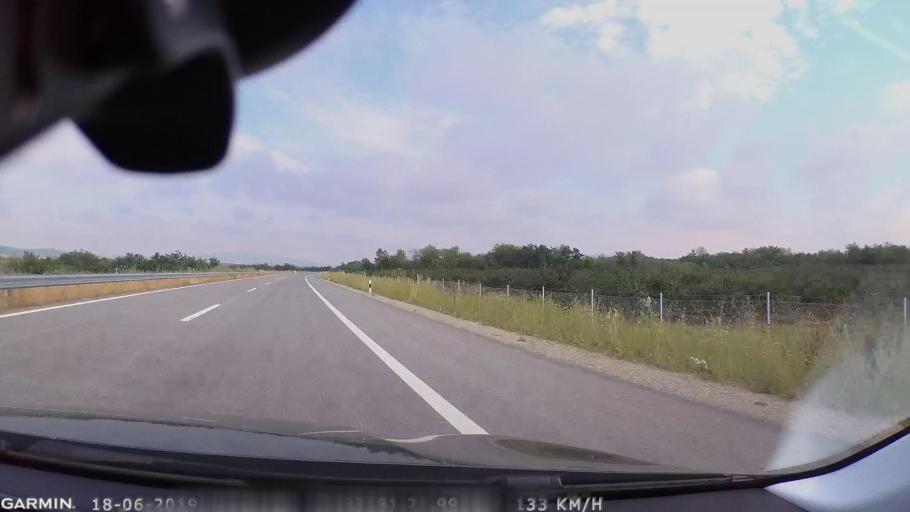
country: MK
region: Sveti Nikole
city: Sveti Nikole
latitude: 41.8321
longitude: 21.9930
